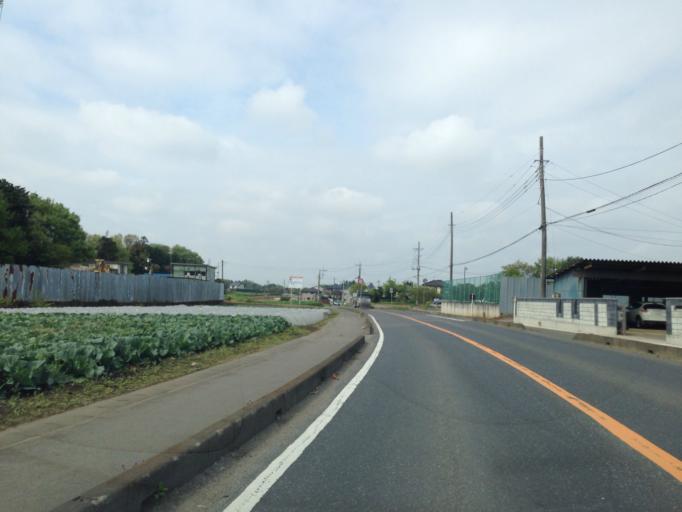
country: JP
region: Ibaraki
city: Sakai
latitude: 36.1703
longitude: 139.8567
